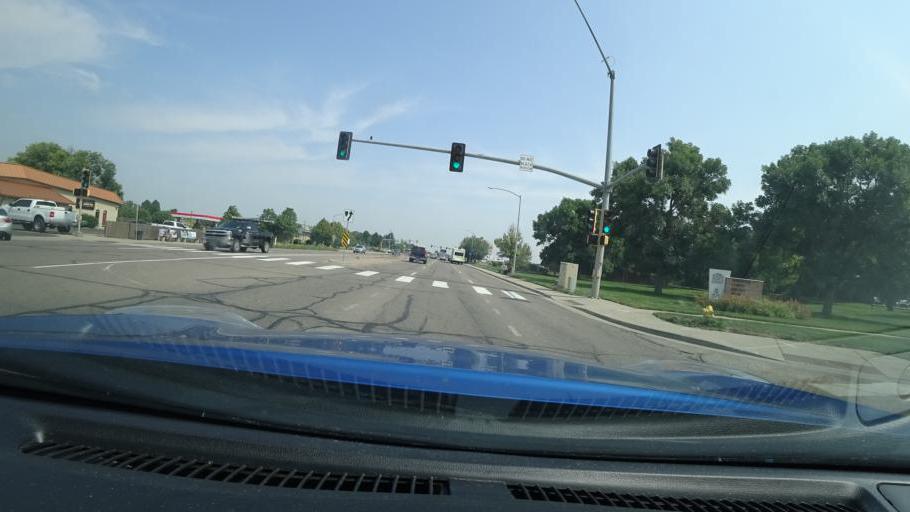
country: US
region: Colorado
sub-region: Adams County
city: Aurora
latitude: 39.7240
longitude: -104.7911
